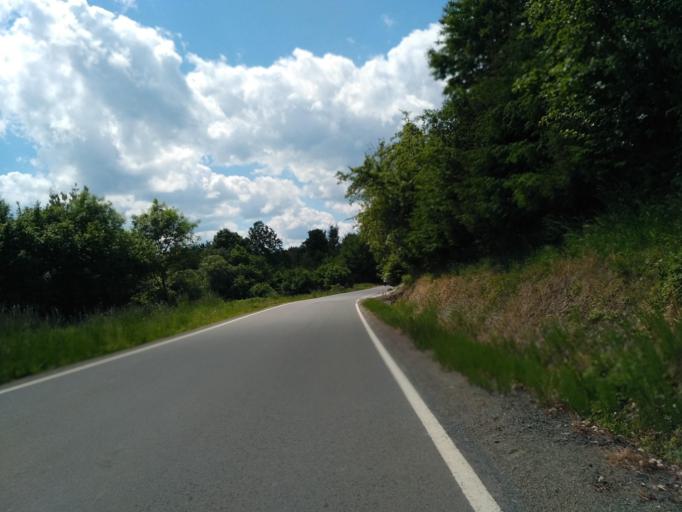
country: PL
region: Subcarpathian Voivodeship
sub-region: Powiat krosnienski
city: Dukla
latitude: 49.5892
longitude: 21.6979
